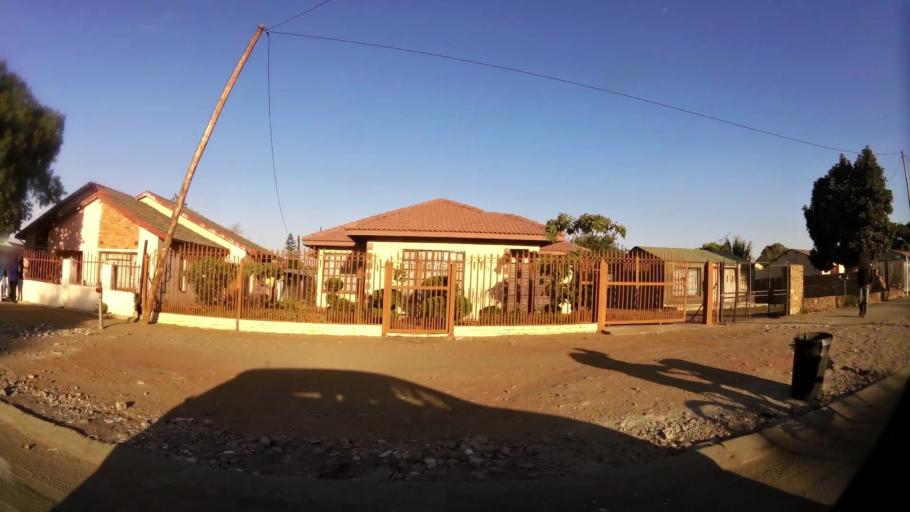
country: ZA
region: North-West
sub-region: Bojanala Platinum District Municipality
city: Rustenburg
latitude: -25.6339
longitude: 27.2148
